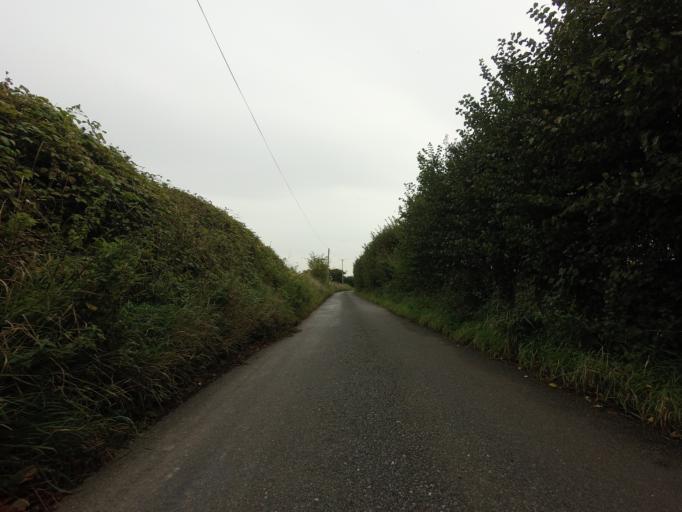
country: GB
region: England
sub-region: Hertfordshire
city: Reed
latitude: 51.9854
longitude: 0.0339
